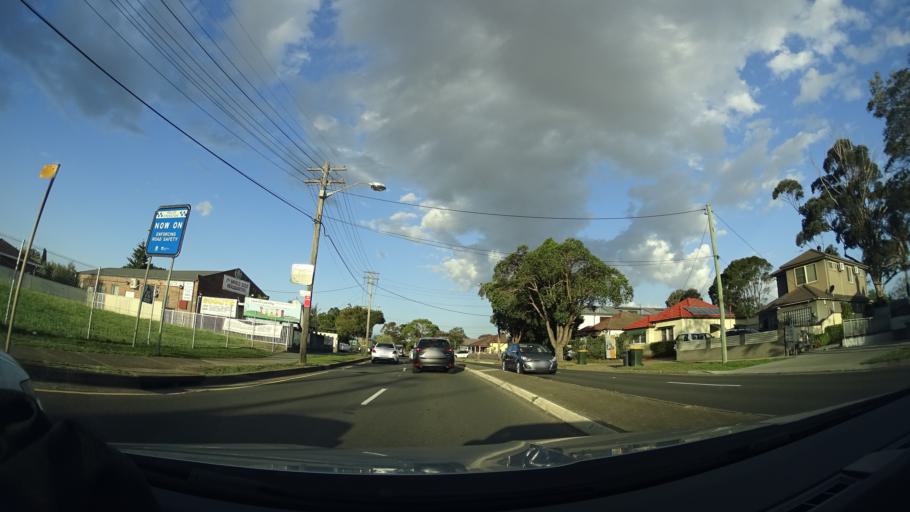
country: AU
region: New South Wales
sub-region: Canterbury
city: Belfield
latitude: -33.8996
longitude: 151.0905
